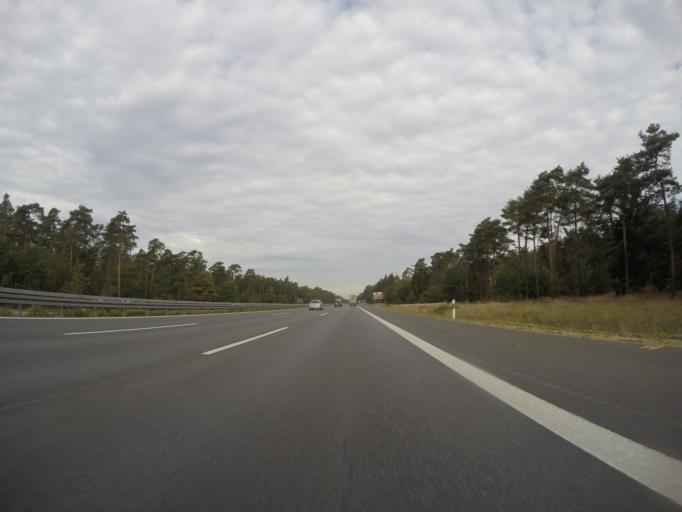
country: DE
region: Bavaria
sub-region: Regierungsbezirk Mittelfranken
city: Wetzendorf
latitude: 49.5179
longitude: 11.0830
